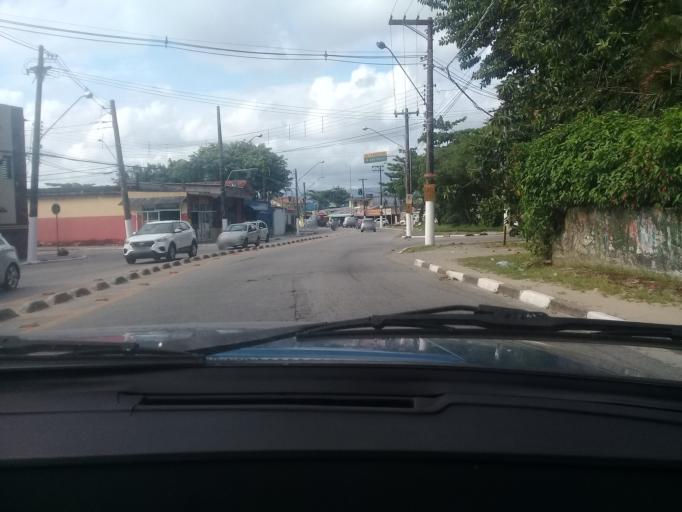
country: BR
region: Sao Paulo
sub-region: Guaruja
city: Guaruja
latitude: -23.9976
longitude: -46.2742
